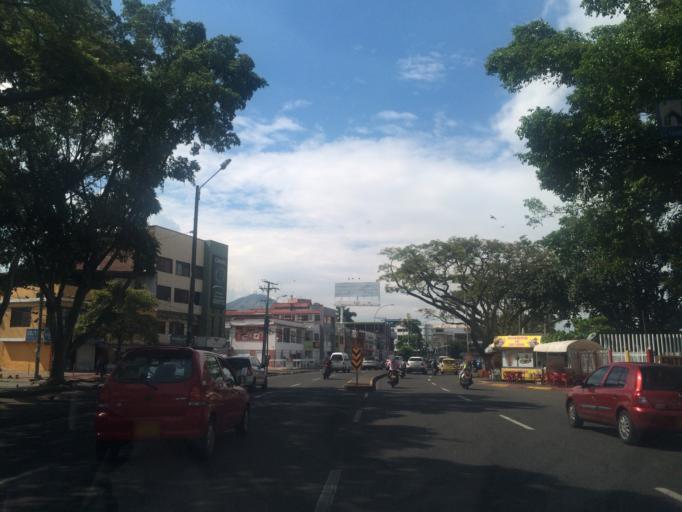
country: CO
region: Valle del Cauca
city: Cali
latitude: 3.4238
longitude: -76.5381
